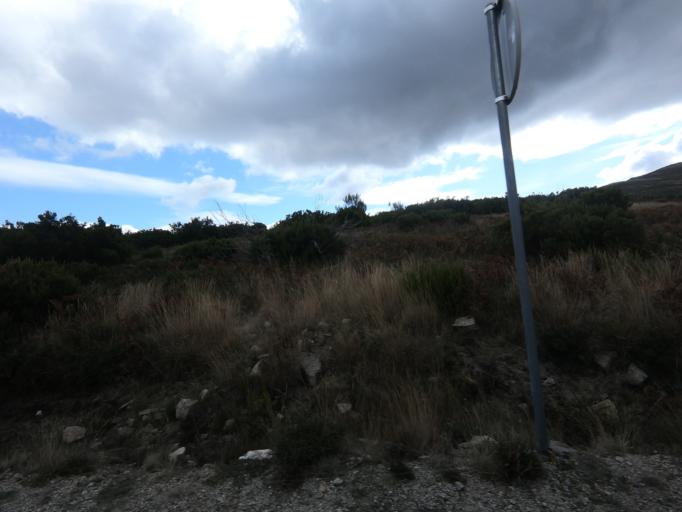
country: PT
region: Vila Real
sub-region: Vila Real
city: Vila Real
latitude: 41.3739
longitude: -7.8089
